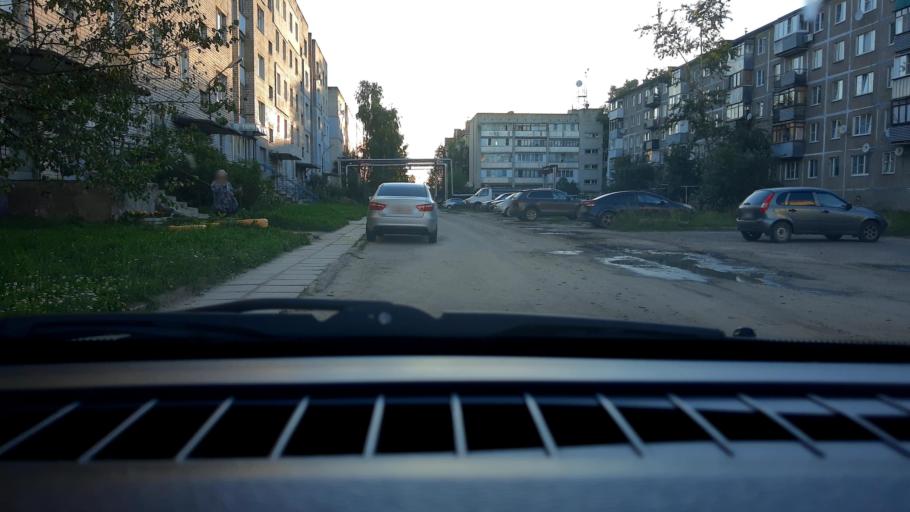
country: RU
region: Nizjnij Novgorod
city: Burevestnik
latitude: 56.1615
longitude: 43.9195
